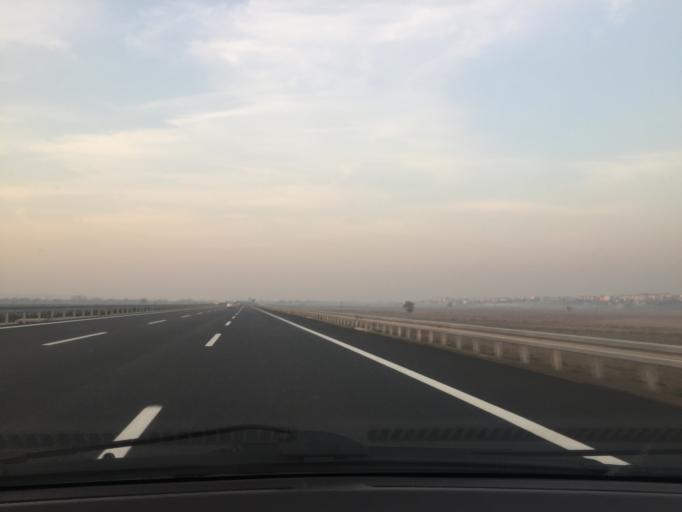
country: TR
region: Bursa
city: Karacabey
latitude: 40.2149
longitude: 28.3924
